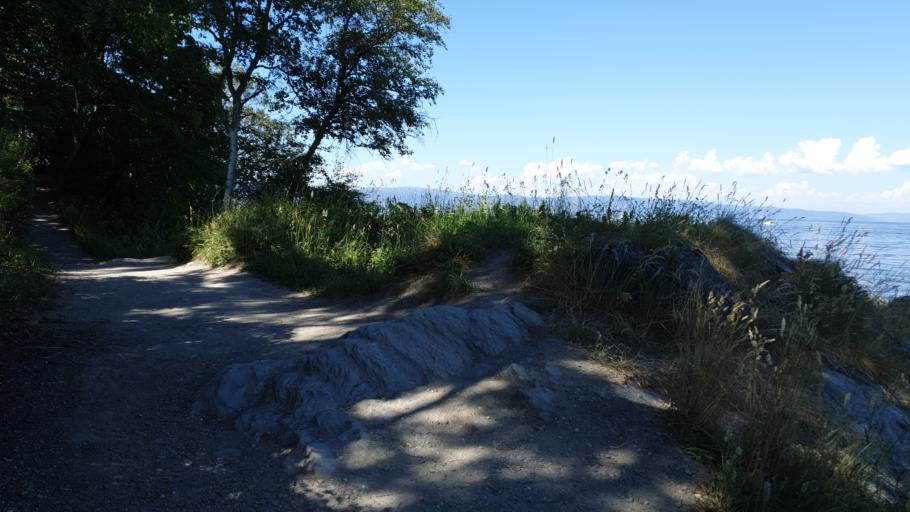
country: NO
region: Sor-Trondelag
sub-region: Trondheim
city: Trondheim
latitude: 63.4535
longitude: 10.4620
